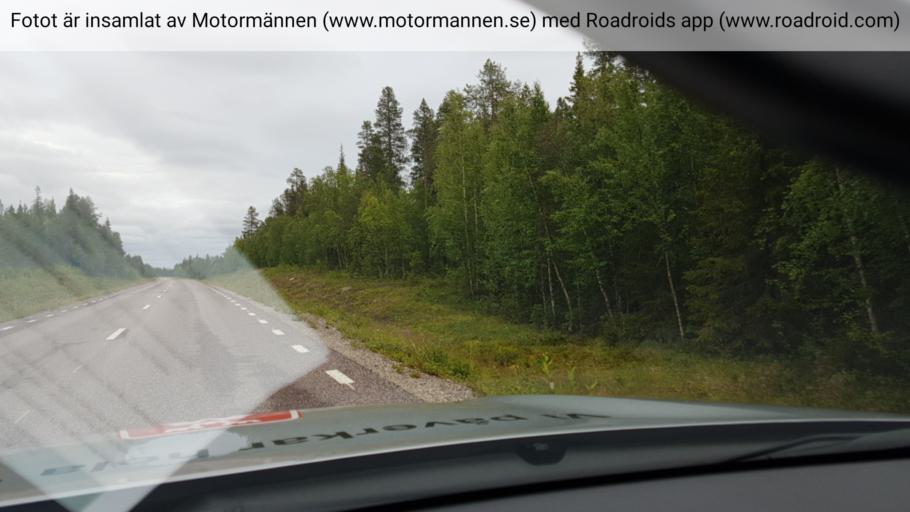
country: SE
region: Norrbotten
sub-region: Gallivare Kommun
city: Gaellivare
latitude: 67.0754
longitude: 21.4366
